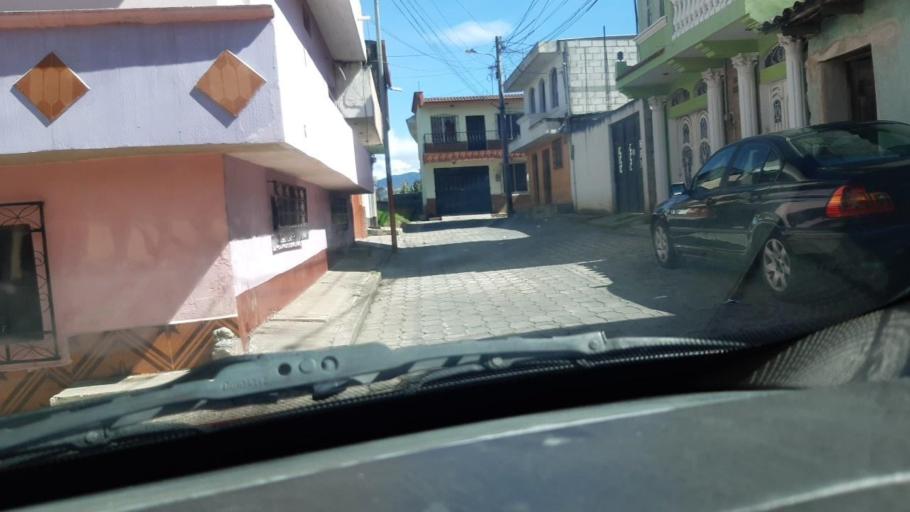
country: GT
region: Quetzaltenango
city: Salcaja
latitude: 14.8807
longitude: -91.4527
